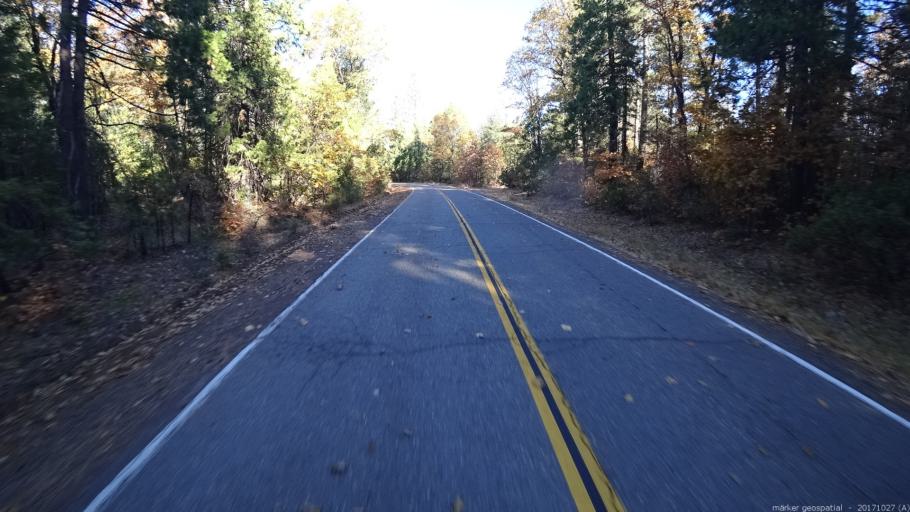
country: US
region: California
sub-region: Shasta County
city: Burney
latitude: 40.9787
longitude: -121.9313
